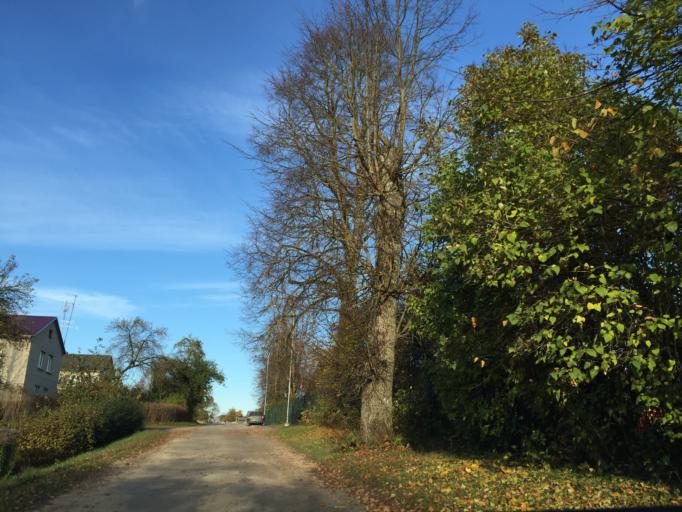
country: LV
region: Skriveri
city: Skriveri
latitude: 56.6252
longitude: 25.1279
